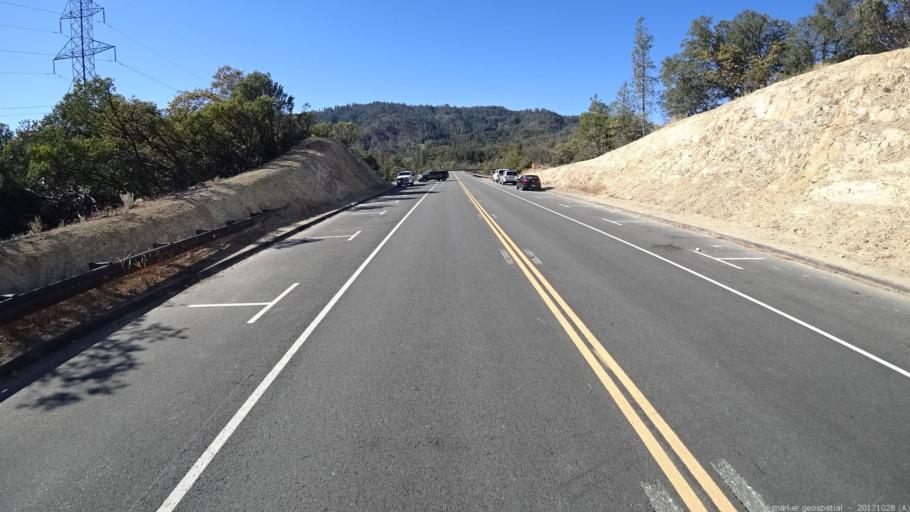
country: US
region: California
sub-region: Shasta County
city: Shasta
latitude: 40.5979
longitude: -122.5432
